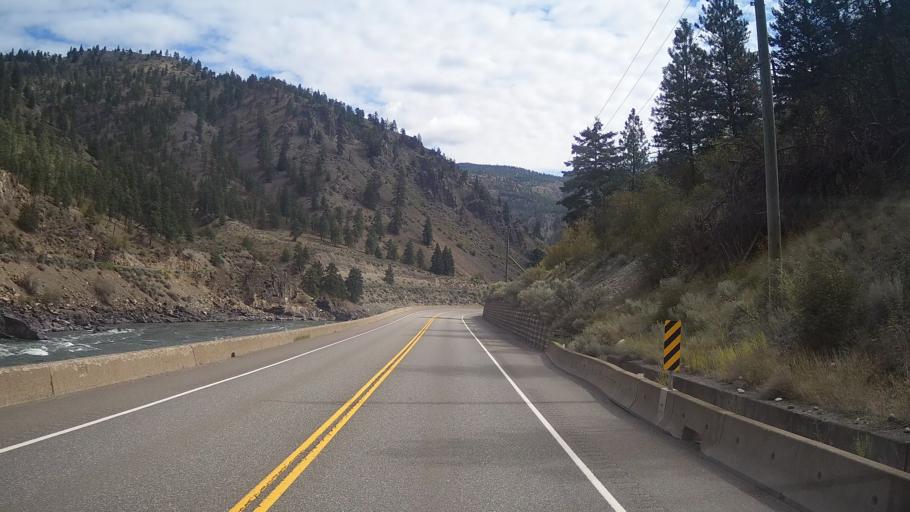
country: CA
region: British Columbia
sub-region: Thompson-Nicola Regional District
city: Ashcroft
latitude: 50.2620
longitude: -121.4194
